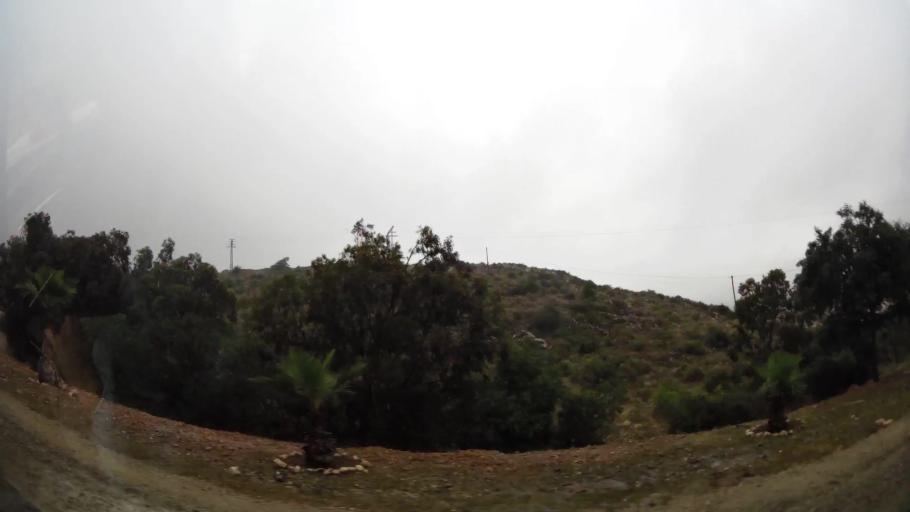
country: MA
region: Taza-Al Hoceima-Taounate
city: Al Hoceima
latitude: 35.2189
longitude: -3.9225
